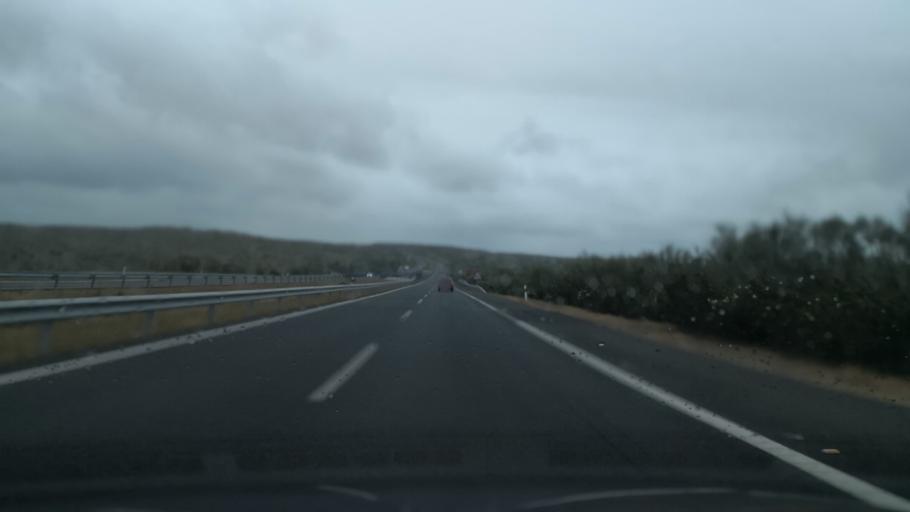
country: ES
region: Extremadura
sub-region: Provincia de Caceres
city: Hinojal
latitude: 39.7232
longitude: -6.4115
